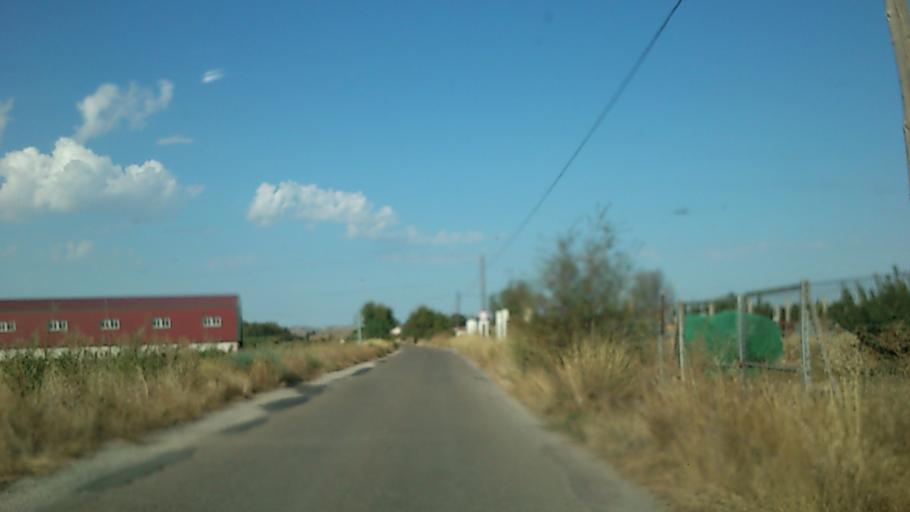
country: ES
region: Aragon
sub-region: Provincia de Zaragoza
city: Villanueva de Gallego
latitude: 41.7324
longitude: -0.8019
